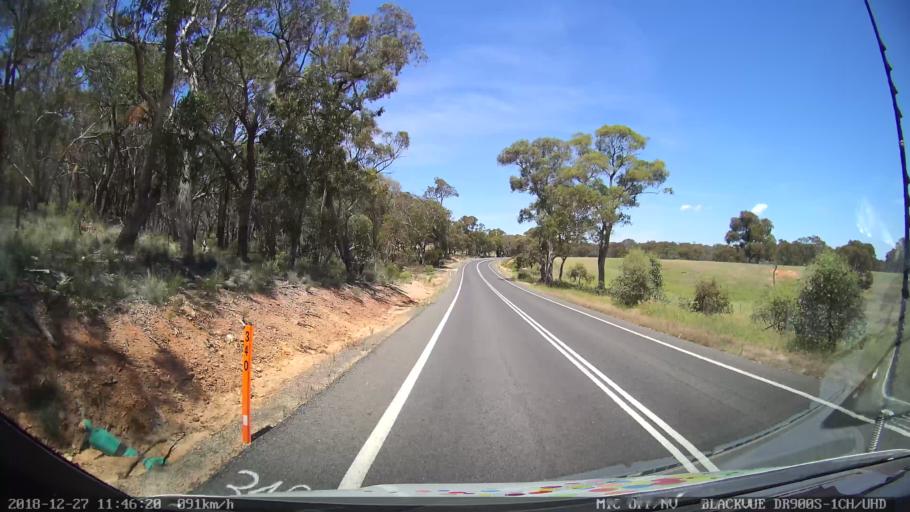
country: AU
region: New South Wales
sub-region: Bathurst Regional
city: Perthville
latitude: -33.5894
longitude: 149.4590
